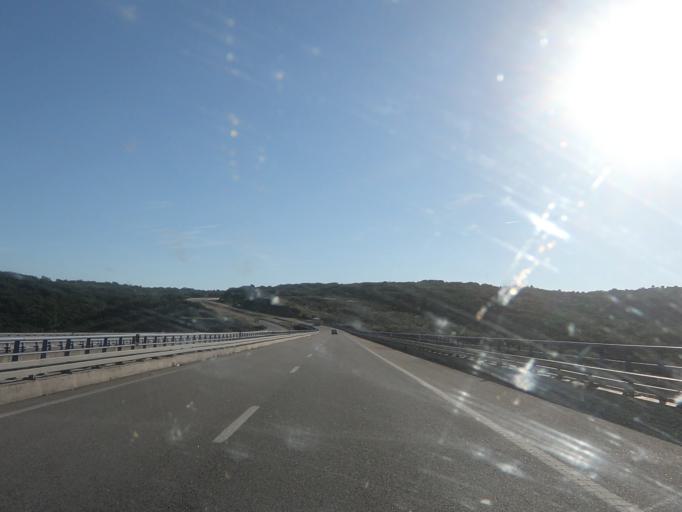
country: ES
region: Castille and Leon
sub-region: Provincia de Salamanca
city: Fuentes de Onoro
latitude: 40.6107
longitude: -6.9187
